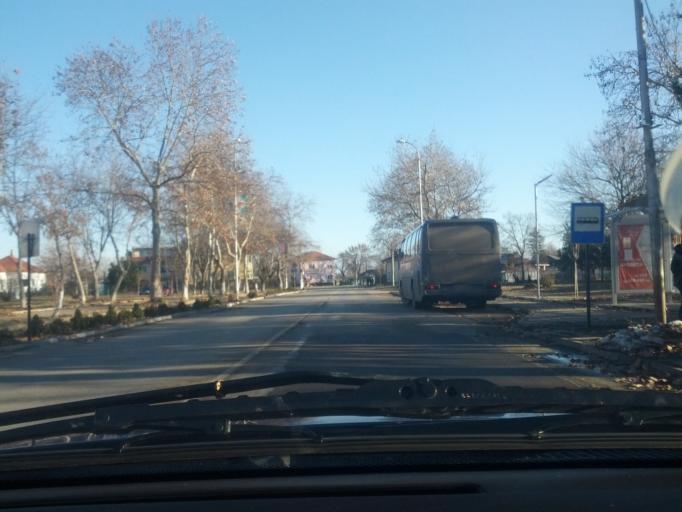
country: BG
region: Vratsa
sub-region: Obshtina Kozloduy
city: Kozloduy
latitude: 43.7749
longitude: 23.7353
